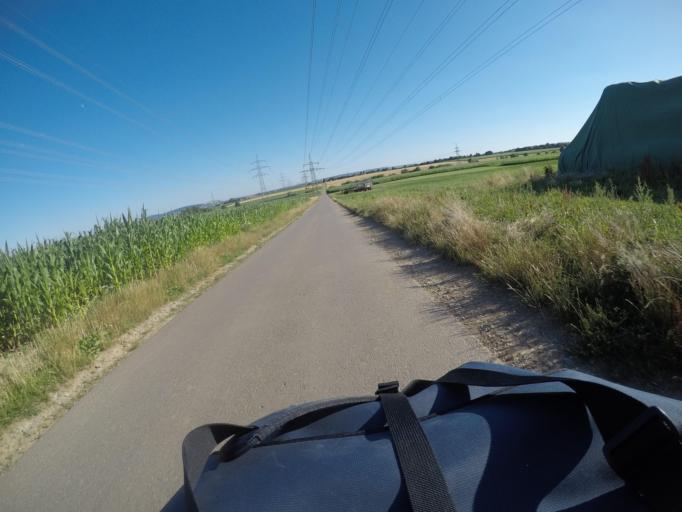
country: DE
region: Baden-Wuerttemberg
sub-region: Regierungsbezirk Stuttgart
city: Stuttgart Muehlhausen
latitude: 48.8796
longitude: 9.2413
